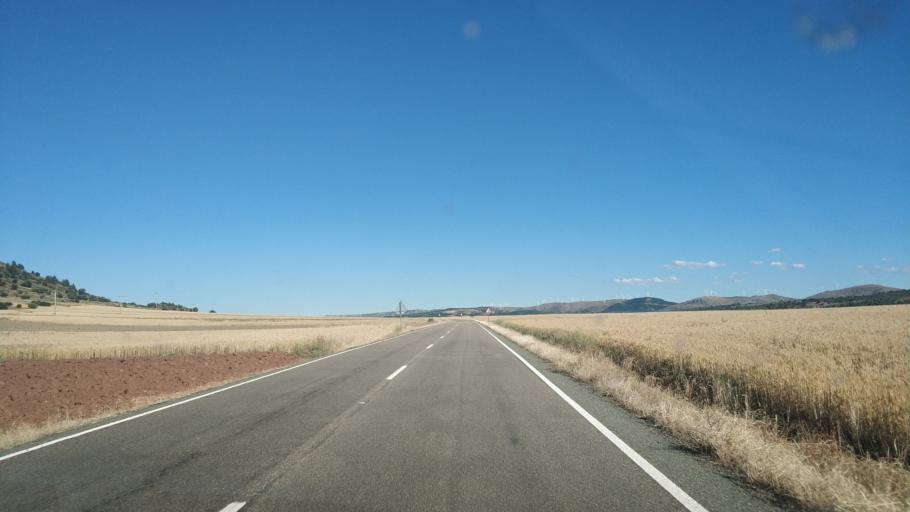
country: ES
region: Castille and Leon
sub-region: Provincia de Soria
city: Montejo de Tiermes
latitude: 41.3558
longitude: -3.1726
